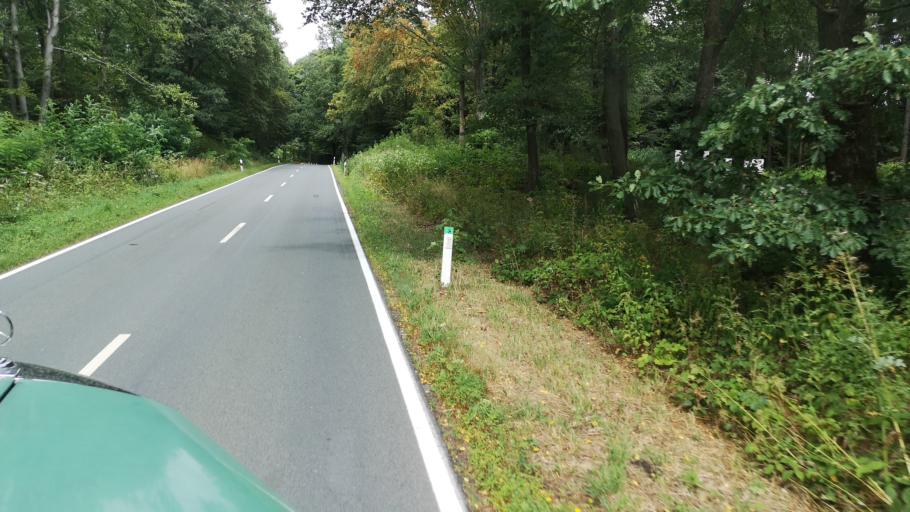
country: DE
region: North Rhine-Westphalia
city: Wermelskirchen
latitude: 51.1176
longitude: 7.2381
